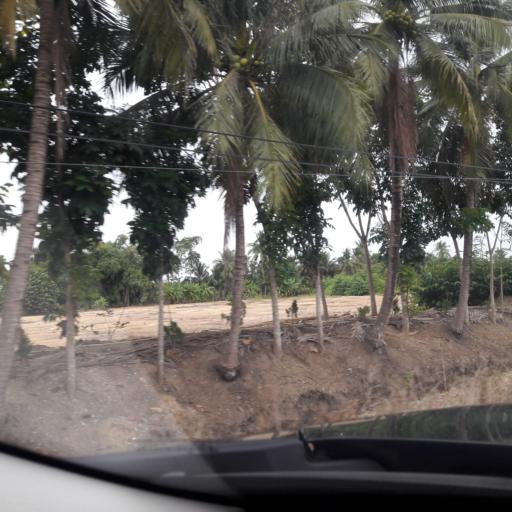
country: TH
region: Ratchaburi
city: Damnoen Saduak
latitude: 13.5613
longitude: 99.9476
